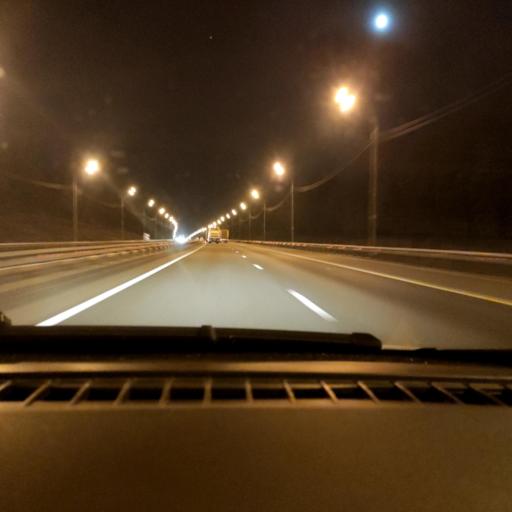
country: RU
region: Lipetsk
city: Khlevnoye
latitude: 52.2225
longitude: 39.1138
